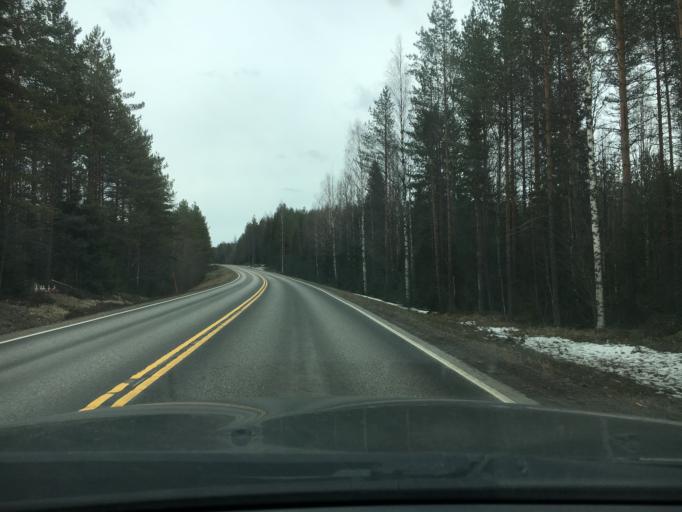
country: FI
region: Central Finland
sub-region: AEaenekoski
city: Sumiainen
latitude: 62.5538
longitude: 26.0073
